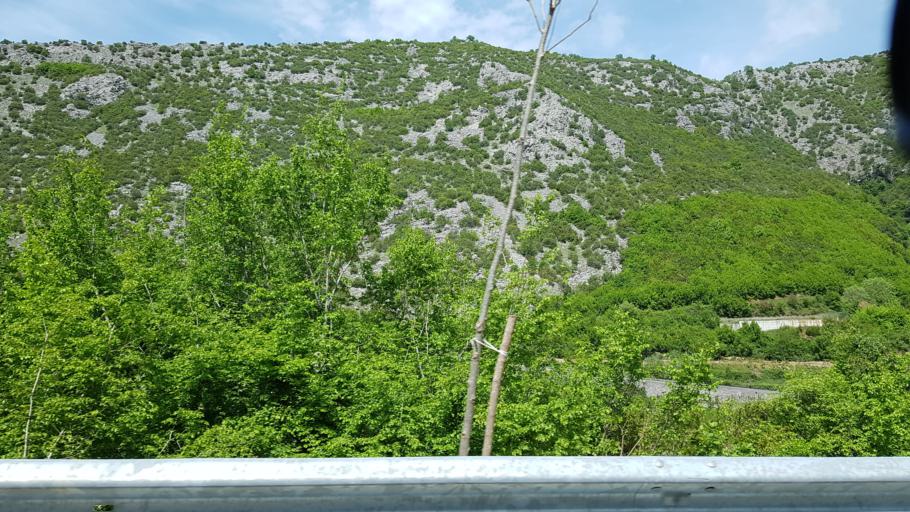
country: AL
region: Shkoder
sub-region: Rrethi i Shkodres
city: Guri i Zi
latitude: 42.1271
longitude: 19.6068
